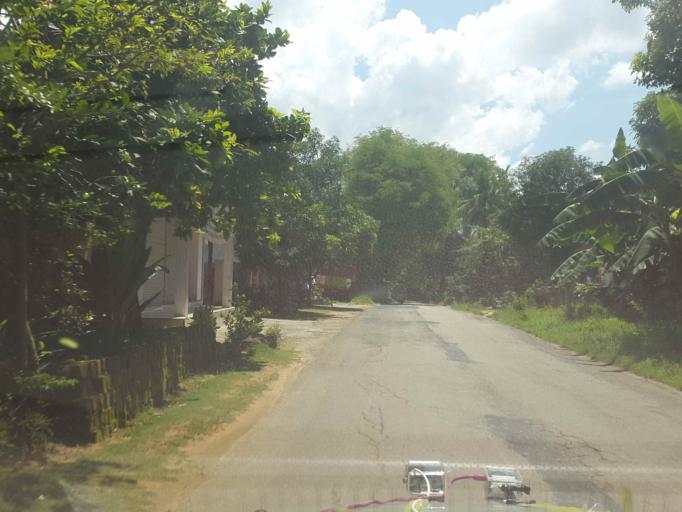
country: ID
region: East Java
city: Giring Barat
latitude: -6.9701
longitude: 113.8648
